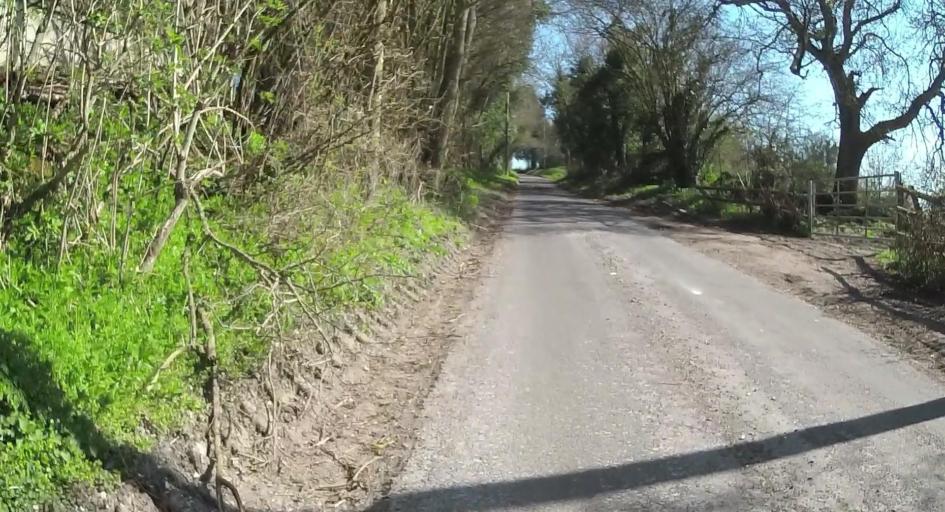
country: GB
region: England
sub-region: Hampshire
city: Highclere
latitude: 51.2754
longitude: -1.3965
